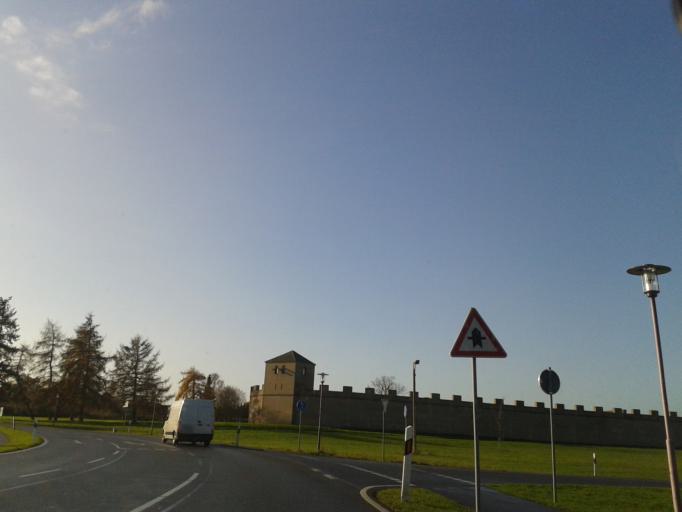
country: DE
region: North Rhine-Westphalia
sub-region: Regierungsbezirk Dusseldorf
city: Xanten
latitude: 51.6683
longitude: 6.4540
